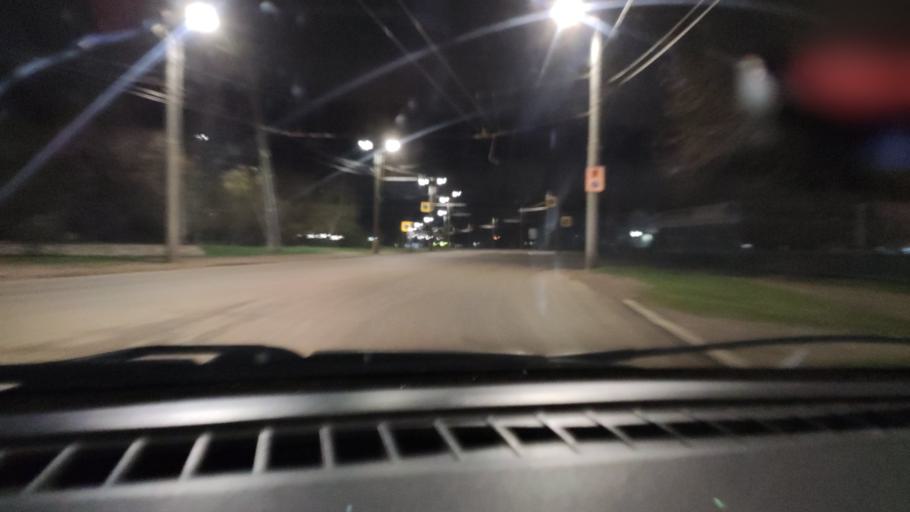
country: RU
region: Bashkortostan
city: Sterlitamak
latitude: 53.6384
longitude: 55.9104
